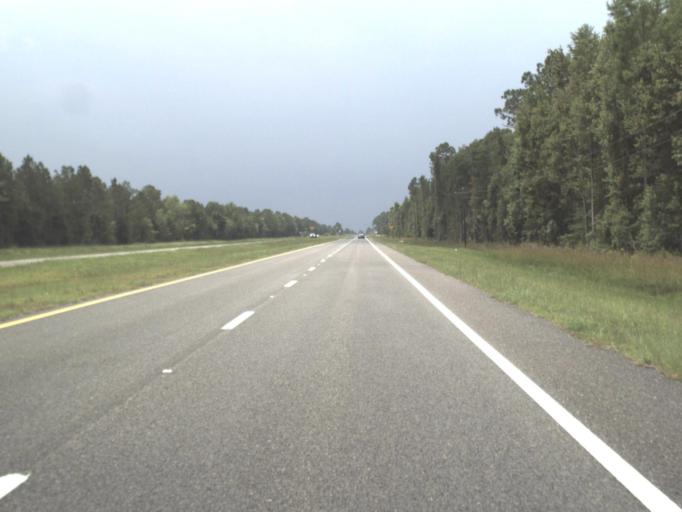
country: US
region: Florida
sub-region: Levy County
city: Chiefland
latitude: 29.3400
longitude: -82.7763
